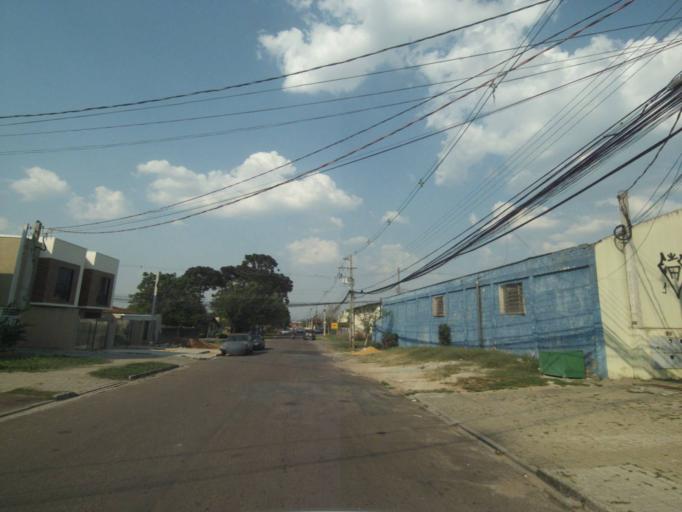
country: BR
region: Parana
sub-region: Sao Jose Dos Pinhais
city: Sao Jose dos Pinhais
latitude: -25.5345
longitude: -49.2359
